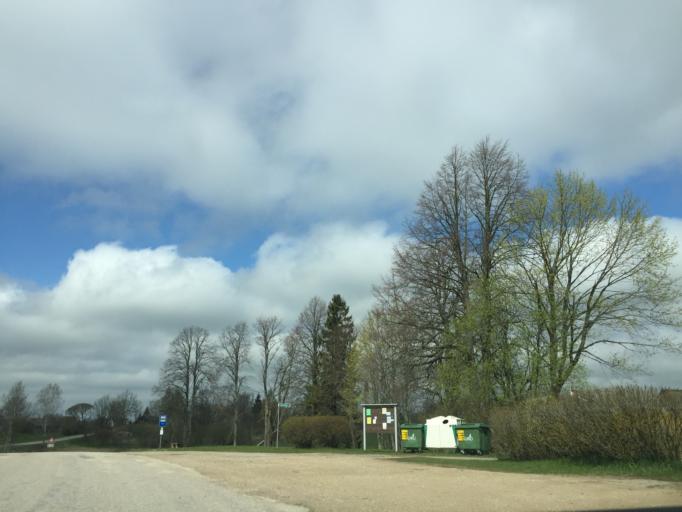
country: EE
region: Valgamaa
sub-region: Valga linn
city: Valga
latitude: 57.5451
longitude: 26.2997
